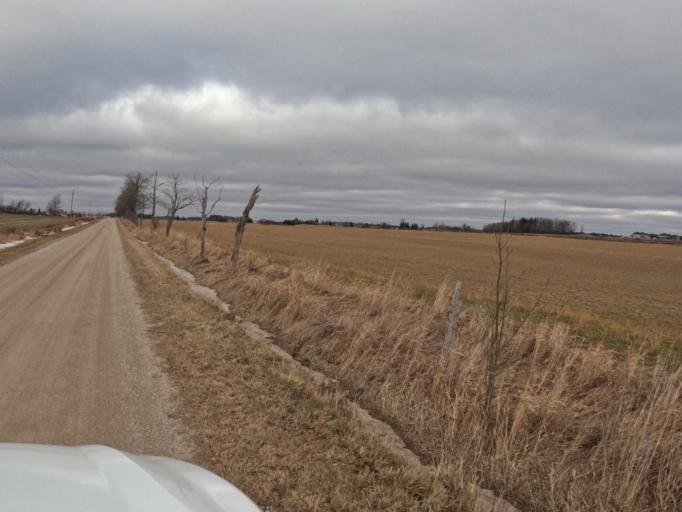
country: CA
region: Ontario
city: Shelburne
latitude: 43.8893
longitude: -80.3287
